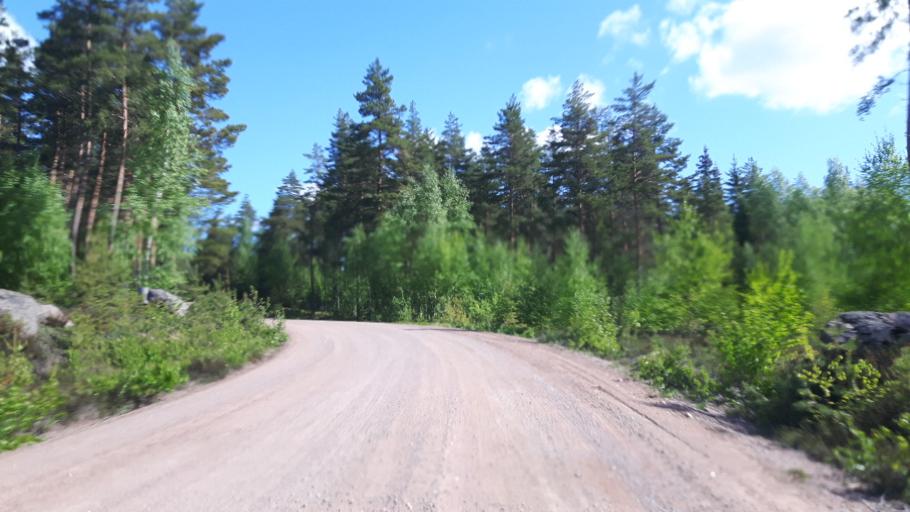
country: FI
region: Kymenlaakso
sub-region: Kotka-Hamina
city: Hamina
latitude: 60.5276
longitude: 27.2844
